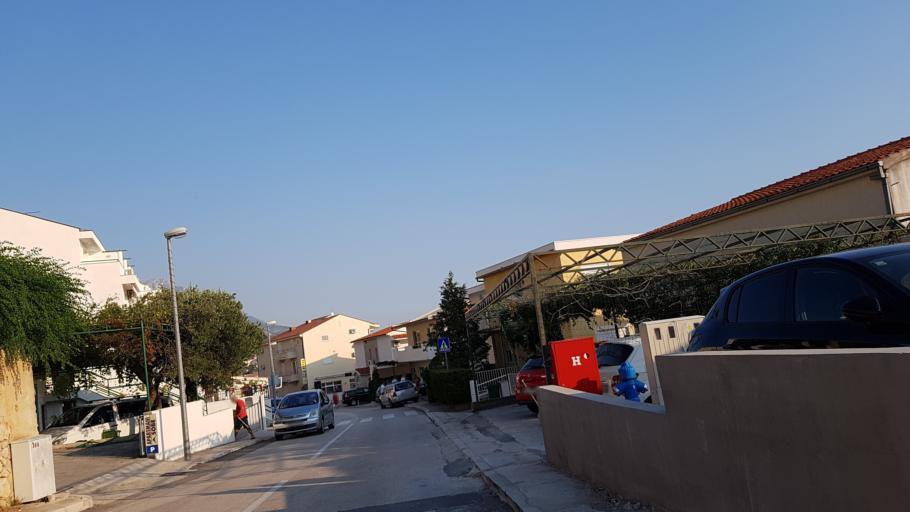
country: HR
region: Splitsko-Dalmatinska
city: Baska Voda
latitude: 43.3609
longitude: 16.9462
